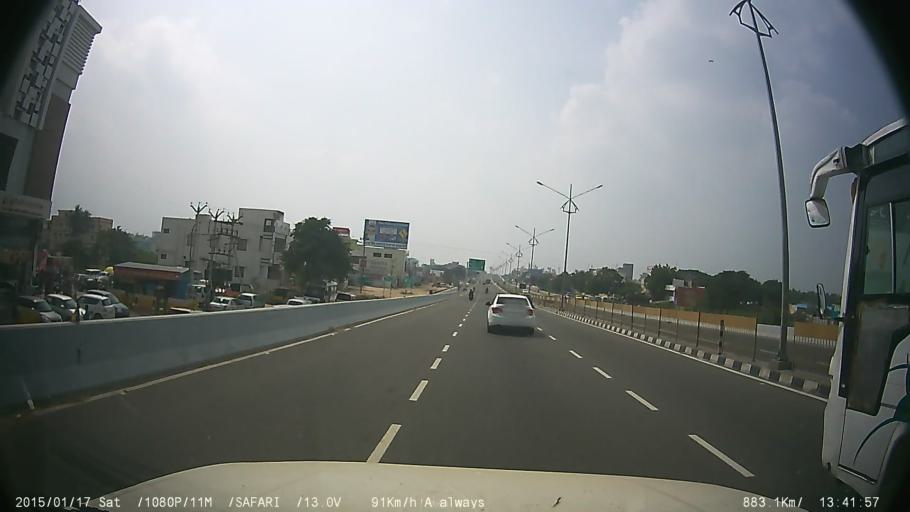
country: IN
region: Tamil Nadu
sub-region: Vellore
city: Vellore
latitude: 12.9347
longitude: 79.1467
